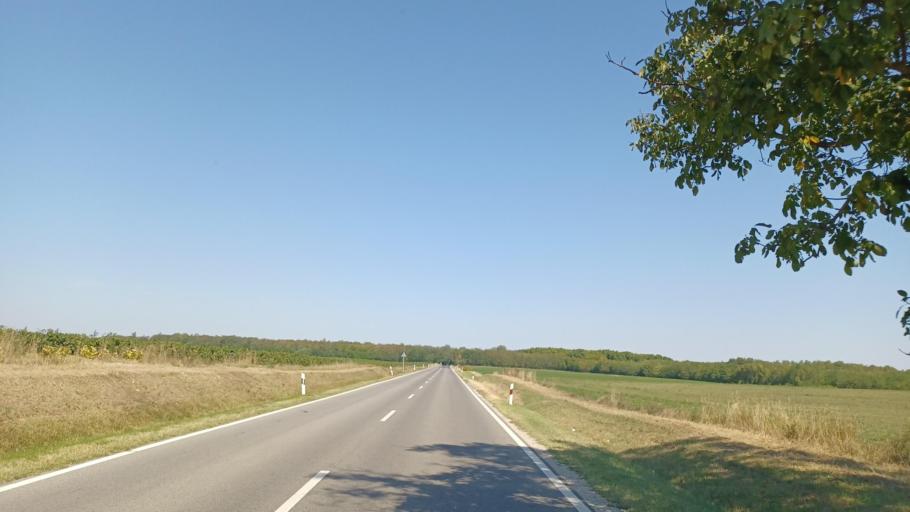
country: HU
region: Tolna
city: Nagydorog
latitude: 46.6874
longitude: 18.6720
